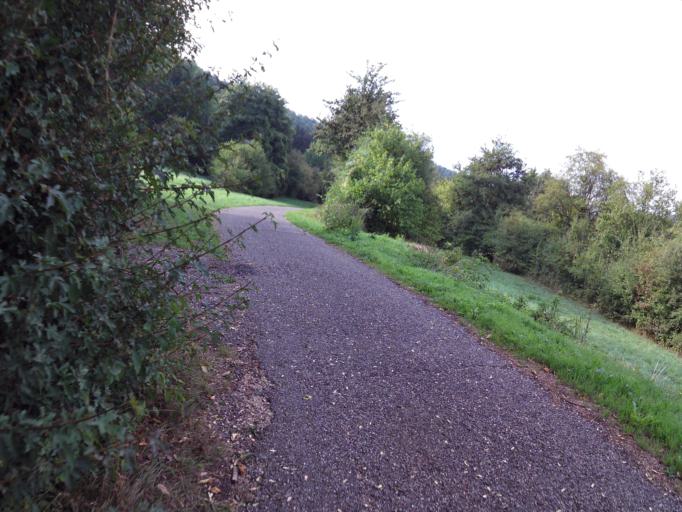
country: DE
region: Rheinland-Pfalz
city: Metterich
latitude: 49.9850
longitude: 6.5725
